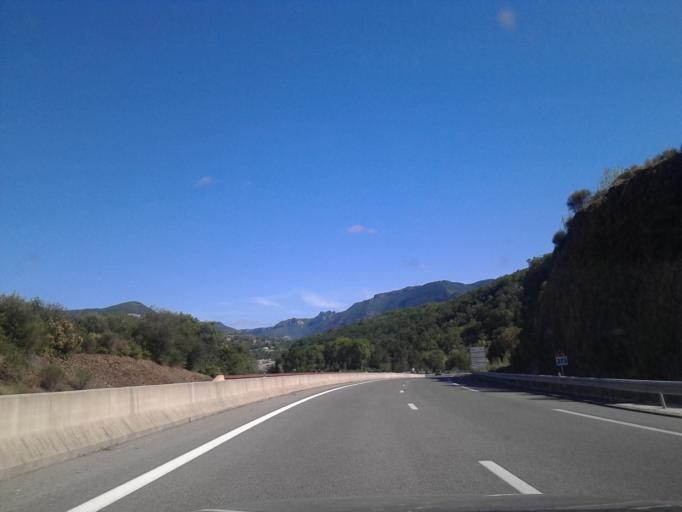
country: FR
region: Languedoc-Roussillon
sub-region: Departement de l'Herault
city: Lodeve
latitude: 43.7445
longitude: 3.3307
